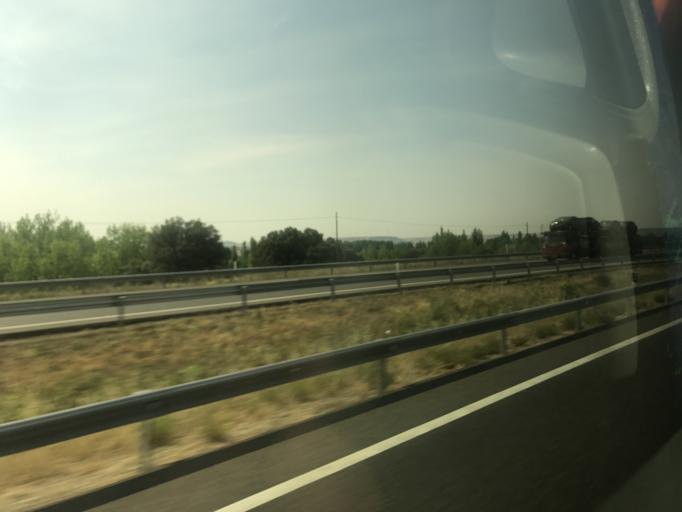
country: ES
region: Castille and Leon
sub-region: Provincia de Palencia
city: Quintana del Puente
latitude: 42.0967
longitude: -4.2037
